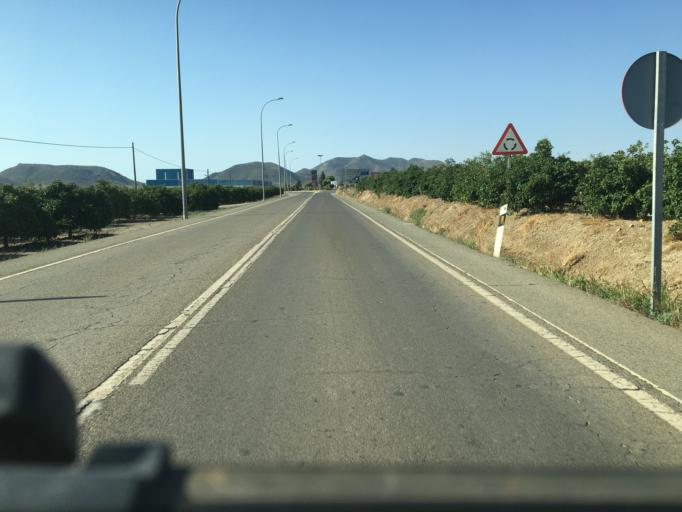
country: ES
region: Murcia
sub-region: Murcia
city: Puerto Lumbreras
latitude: 37.5412
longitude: -1.8140
